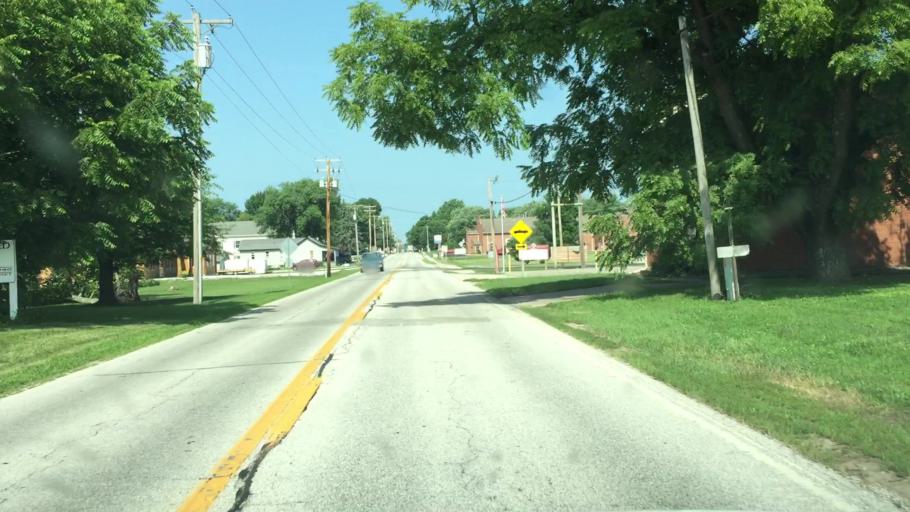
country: US
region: Illinois
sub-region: Hancock County
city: Nauvoo
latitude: 40.5496
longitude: -91.3696
